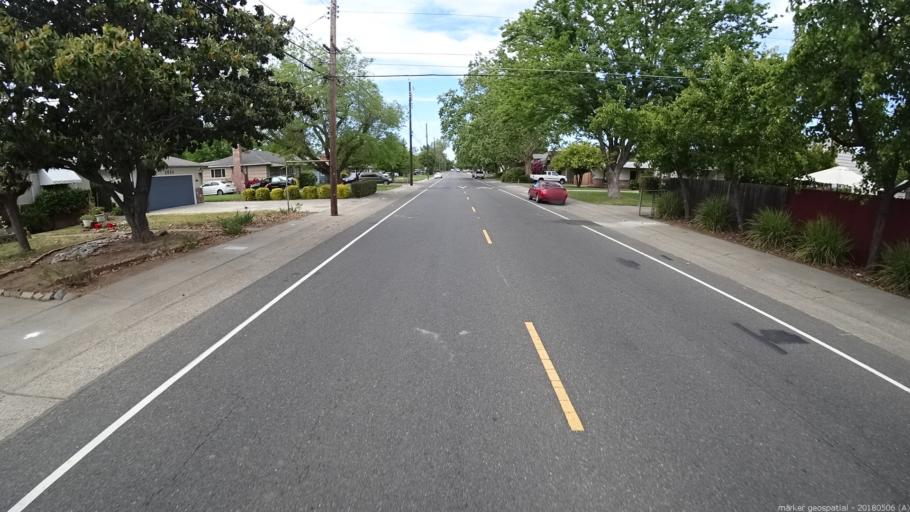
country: US
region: California
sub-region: Sacramento County
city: Parkway
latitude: 38.5478
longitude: -121.4366
